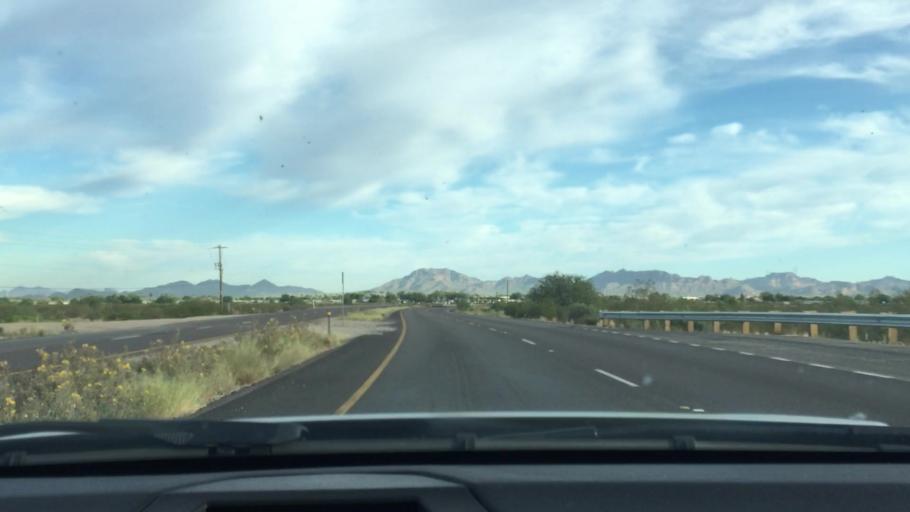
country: US
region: Arizona
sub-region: Pinal County
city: Apache Junction
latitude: 33.3728
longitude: -111.5627
